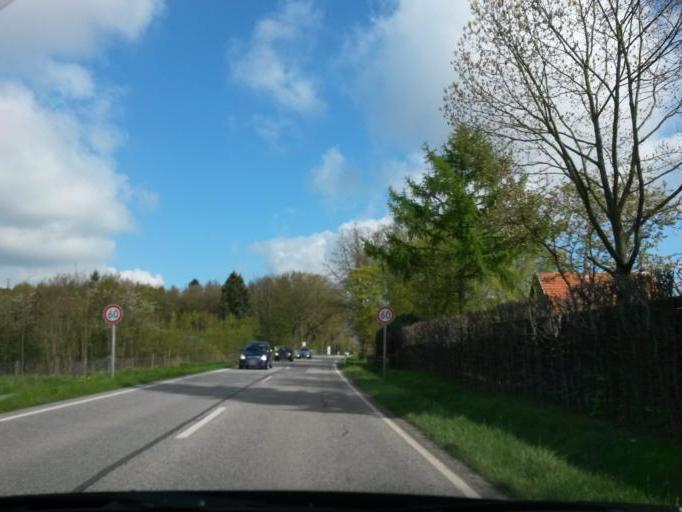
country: DE
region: Schleswig-Holstein
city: Holm
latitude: 53.6009
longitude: 9.6797
